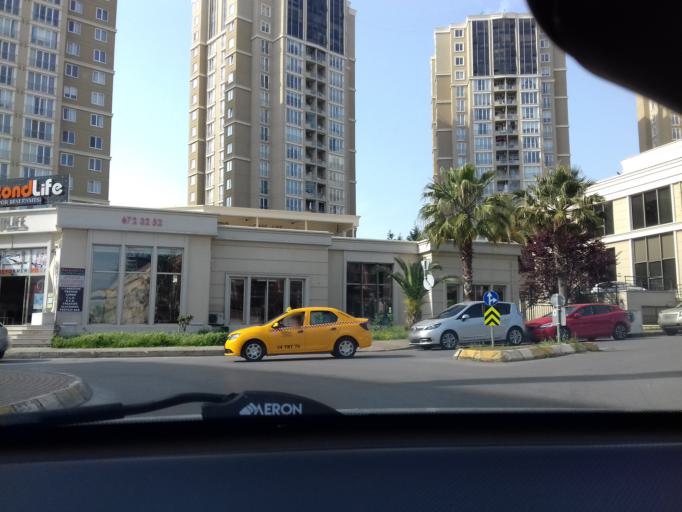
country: TR
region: Istanbul
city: Maltepe
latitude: 40.9130
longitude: 29.2101
